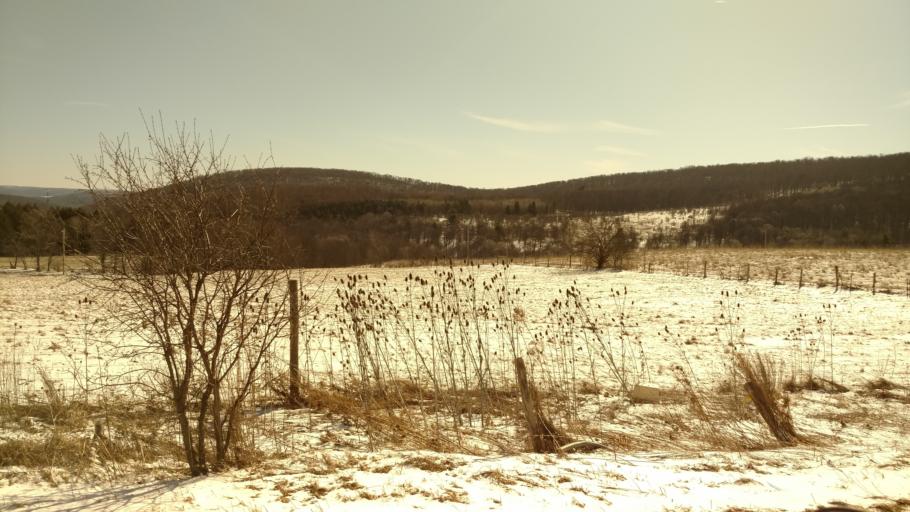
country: US
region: New York
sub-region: Allegany County
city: Wellsville
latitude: 42.0716
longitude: -78.0097
